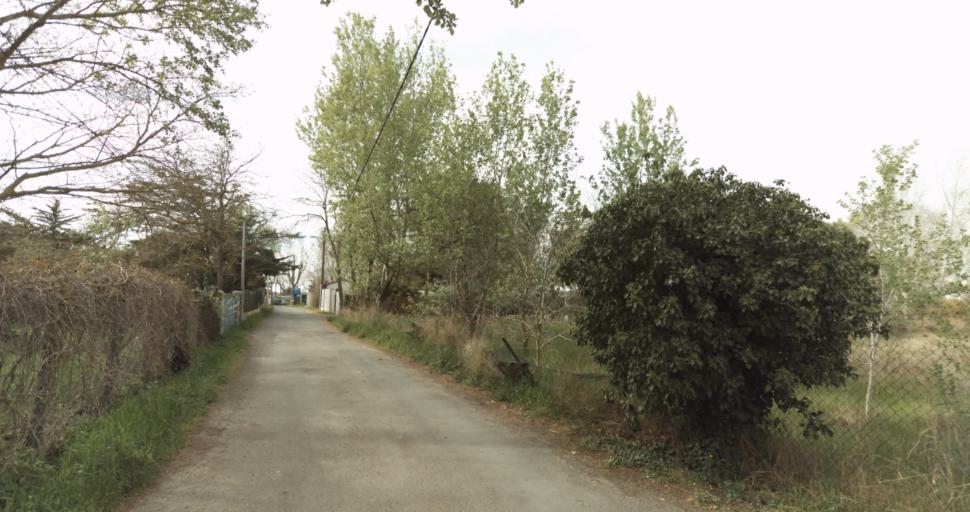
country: FR
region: Languedoc-Roussillon
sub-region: Departement de l'Herault
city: Marseillan
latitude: 43.3277
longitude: 3.5481
